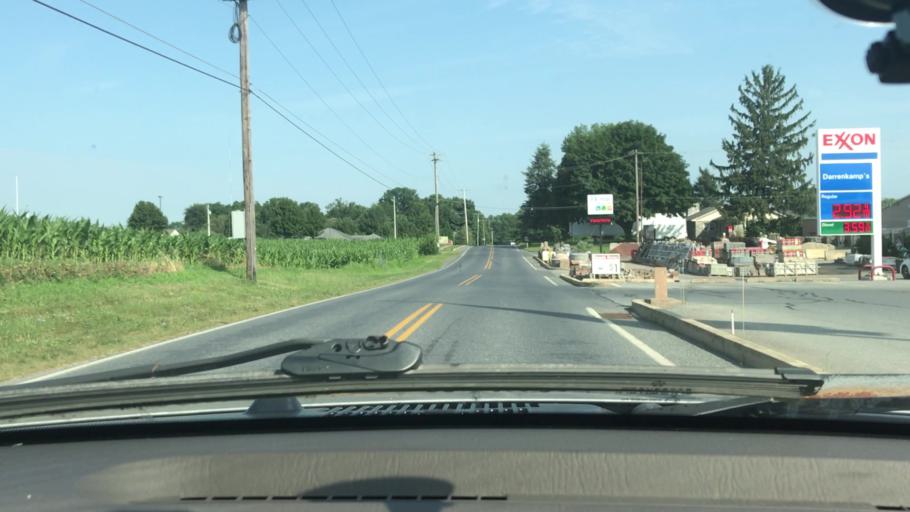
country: US
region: Pennsylvania
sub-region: Lancaster County
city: Elizabethtown
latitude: 40.1620
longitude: -76.5735
